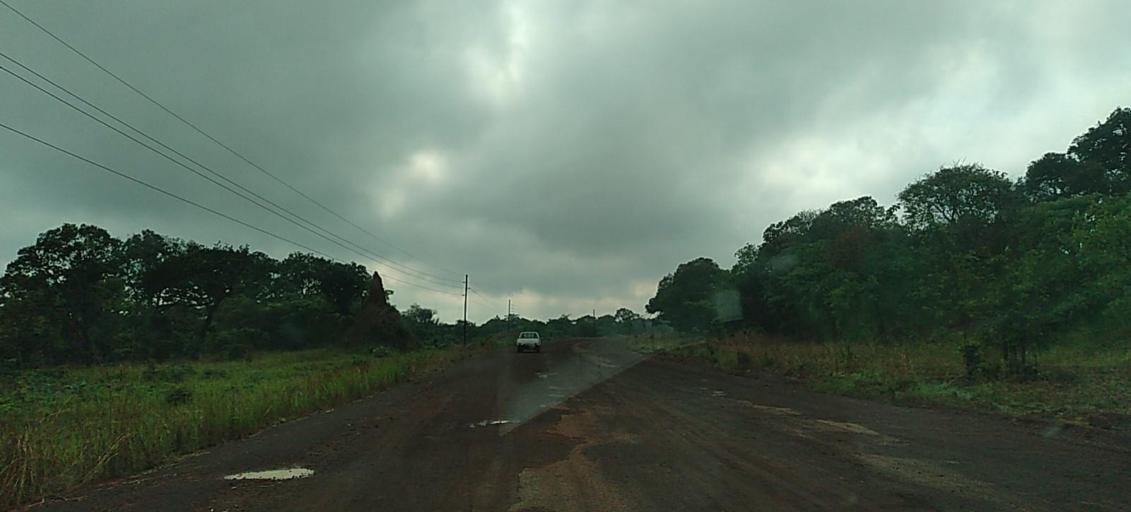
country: ZM
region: North-Western
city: Mwinilunga
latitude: -11.7254
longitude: 24.5736
